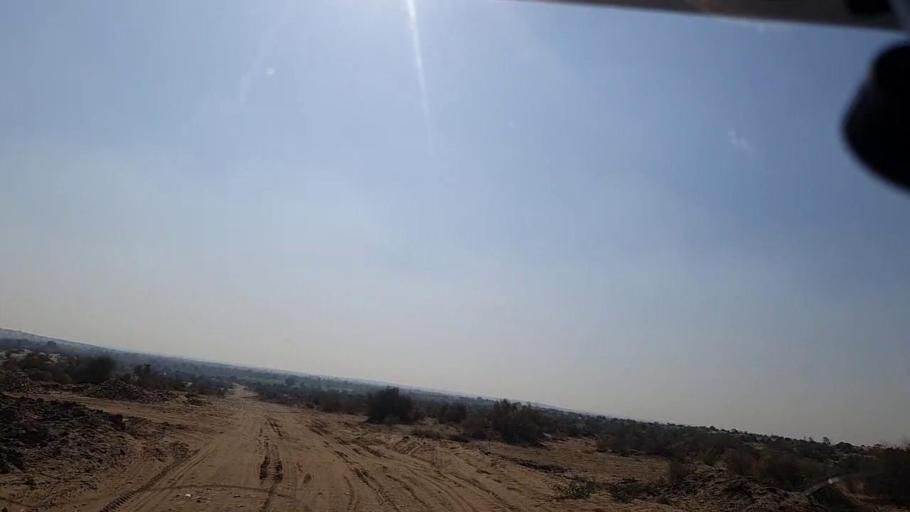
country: PK
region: Sindh
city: Khanpur
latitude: 27.5582
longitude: 69.3866
